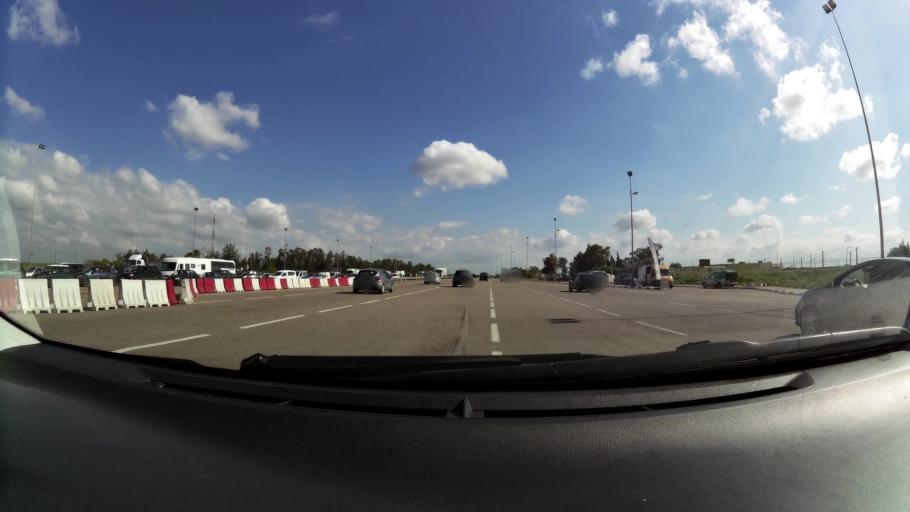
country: MA
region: Chaouia-Ouardigha
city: Nouaseur
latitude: 33.3676
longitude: -7.6205
